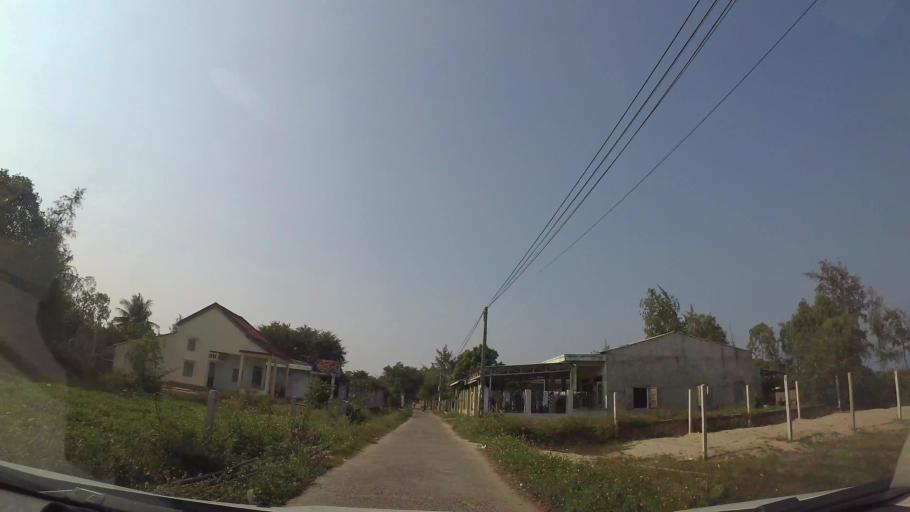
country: VN
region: Da Nang
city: Ngu Hanh Son
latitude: 15.9533
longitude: 108.2660
